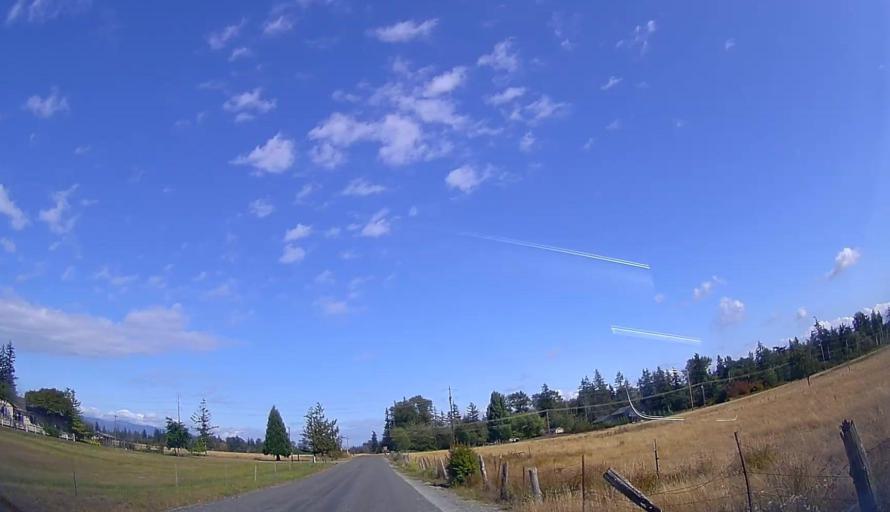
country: US
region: Washington
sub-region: Skagit County
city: Burlington
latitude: 48.4939
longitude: -122.4467
